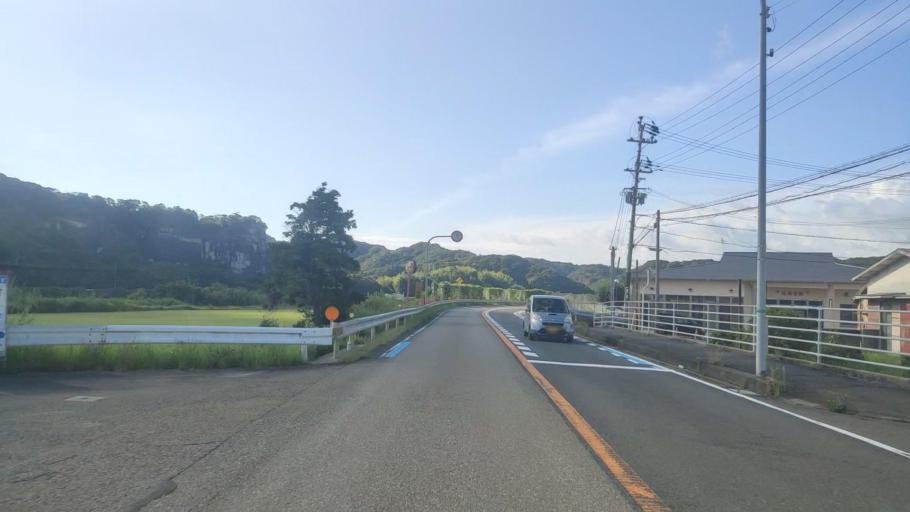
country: JP
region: Wakayama
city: Tanabe
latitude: 33.6614
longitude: 135.3990
